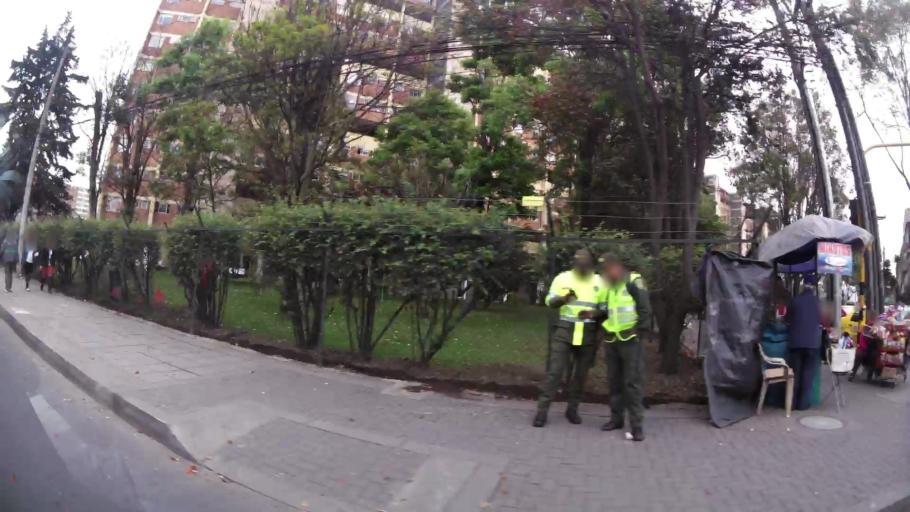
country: CO
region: Bogota D.C.
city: Bogota
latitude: 4.6282
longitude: -74.0909
